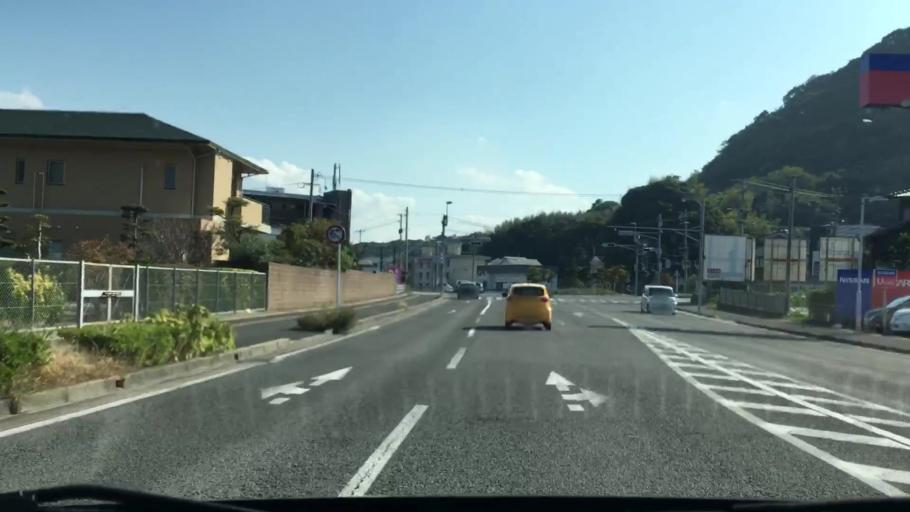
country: JP
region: Nagasaki
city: Togitsu
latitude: 32.8475
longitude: 129.8306
